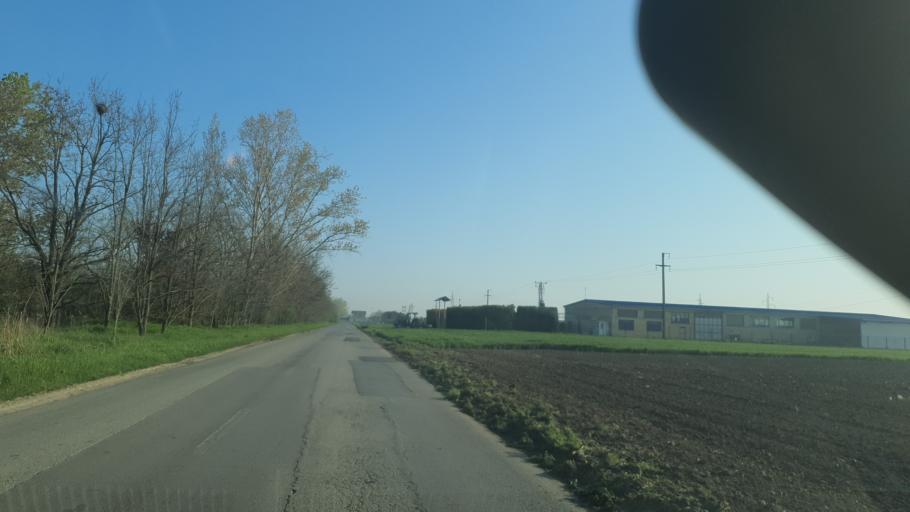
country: RS
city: Rumenka
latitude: 45.2625
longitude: 19.7005
